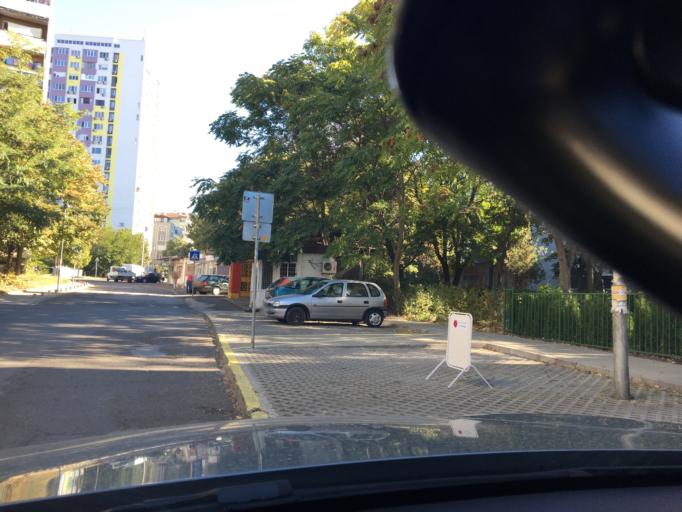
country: BG
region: Burgas
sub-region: Obshtina Burgas
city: Burgas
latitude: 42.5196
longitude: 27.4483
